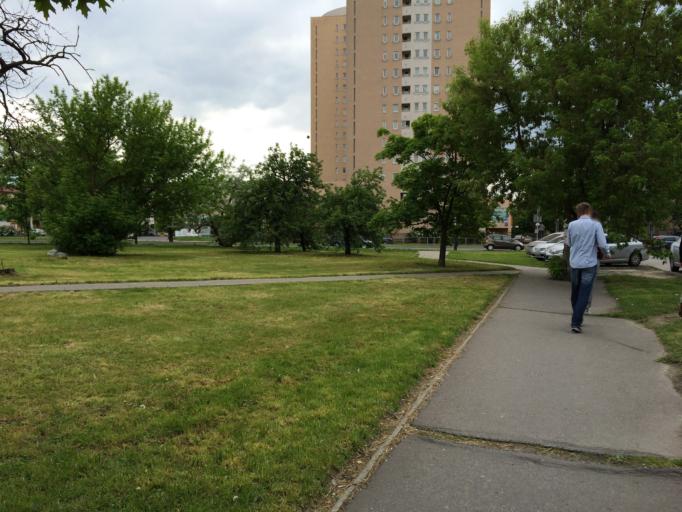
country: PL
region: Masovian Voivodeship
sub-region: Warszawa
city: Praga Poludnie
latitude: 52.2352
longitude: 21.0999
